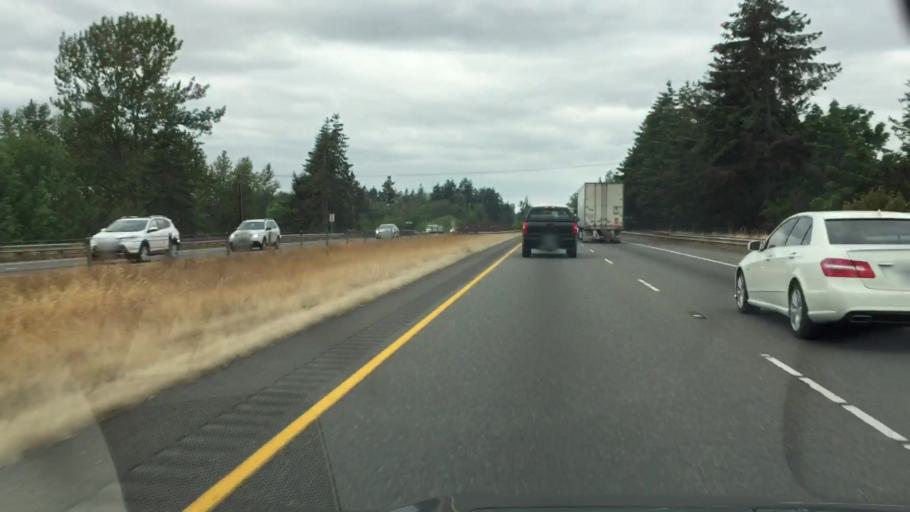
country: US
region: Washington
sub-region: Pierce County
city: Midland
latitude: 47.1583
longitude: -122.3871
